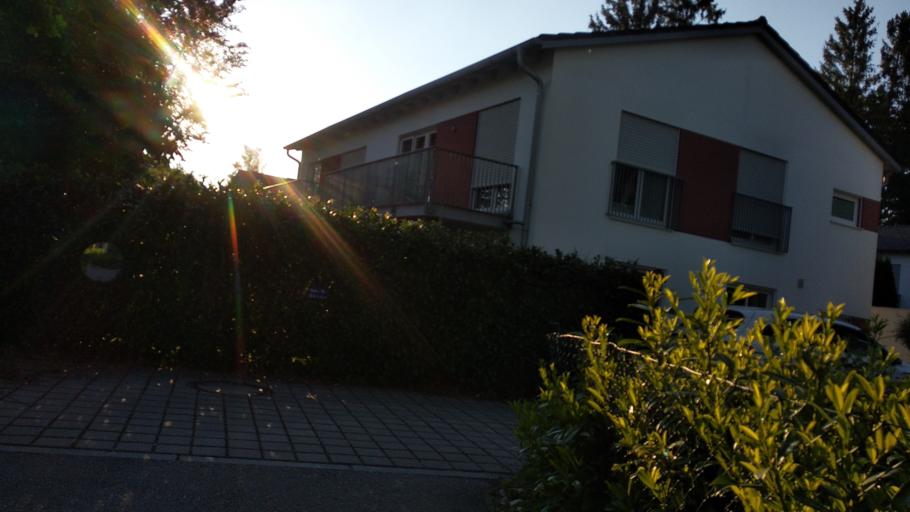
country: DE
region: Bavaria
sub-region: Upper Bavaria
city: Zorneding
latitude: 48.0963
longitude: 11.7969
